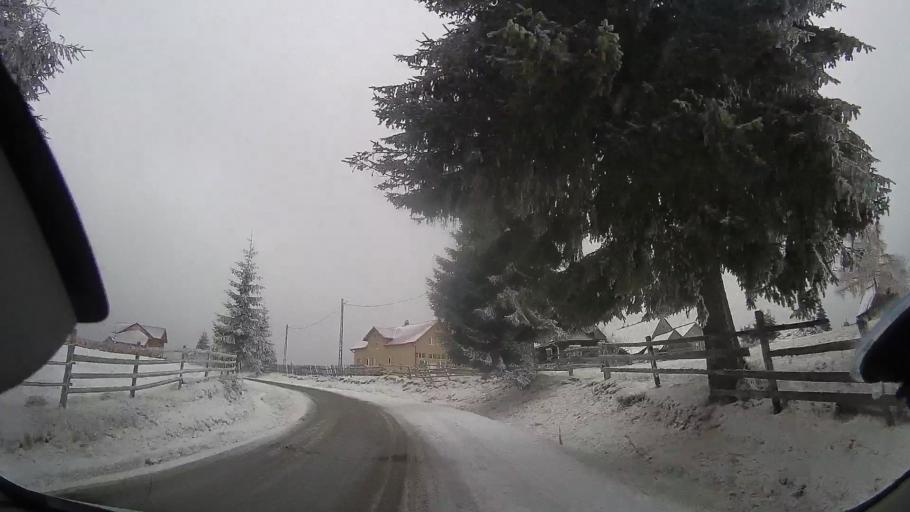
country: RO
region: Cluj
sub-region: Comuna Maguri-Racatau
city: Maguri
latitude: 46.6545
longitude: 23.0846
